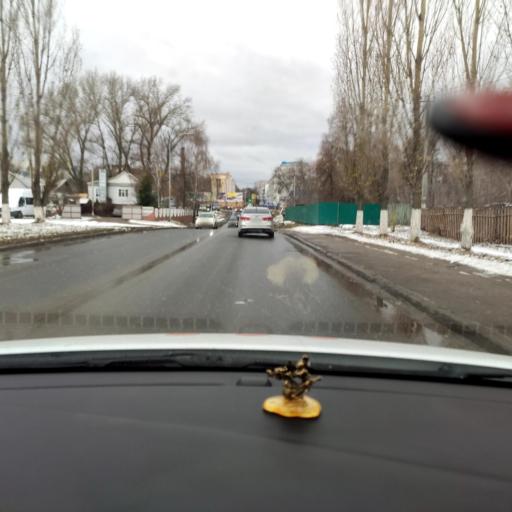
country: RU
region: Tatarstan
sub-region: Zelenodol'skiy Rayon
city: Zelenodolsk
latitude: 55.8480
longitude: 48.5277
